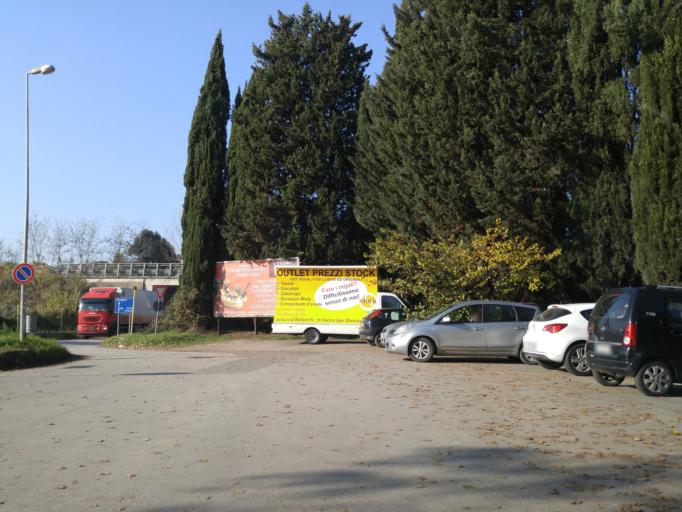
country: IT
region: The Marches
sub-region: Provincia di Pesaro e Urbino
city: Calcinelli
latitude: 43.7482
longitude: 12.9232
